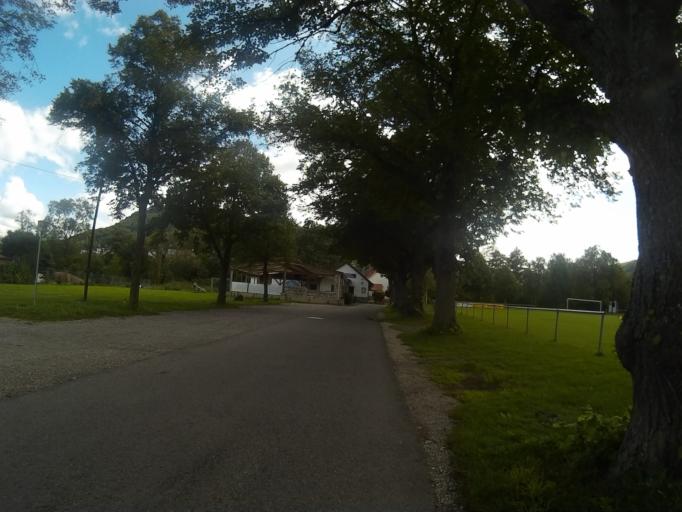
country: DE
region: Baden-Wuerttemberg
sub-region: Tuebingen Region
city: Pfullingen
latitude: 48.4540
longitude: 9.2094
